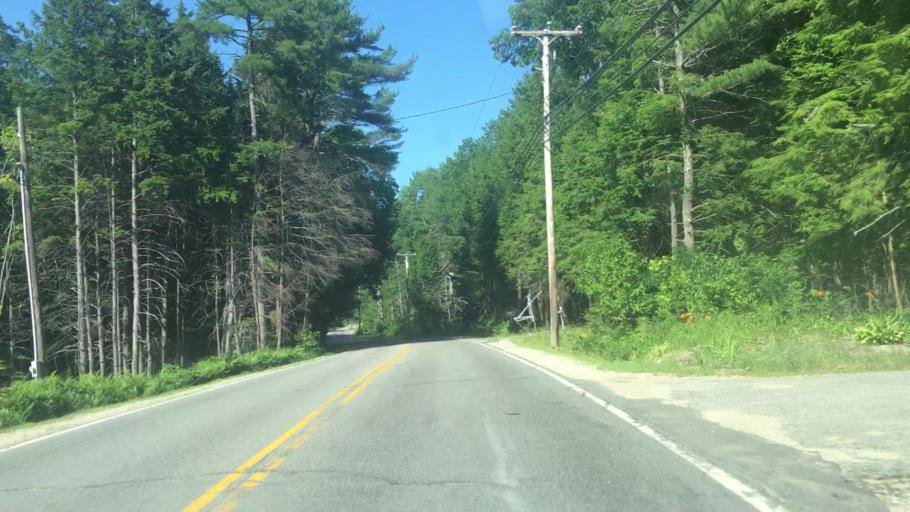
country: US
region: Maine
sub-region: York County
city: Hollis Center
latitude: 43.6752
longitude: -70.5937
